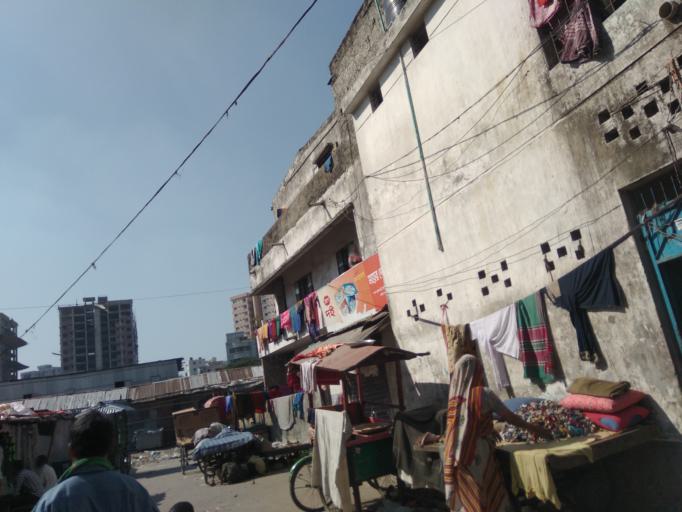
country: BD
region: Dhaka
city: Azimpur
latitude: 23.7711
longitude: 90.3621
